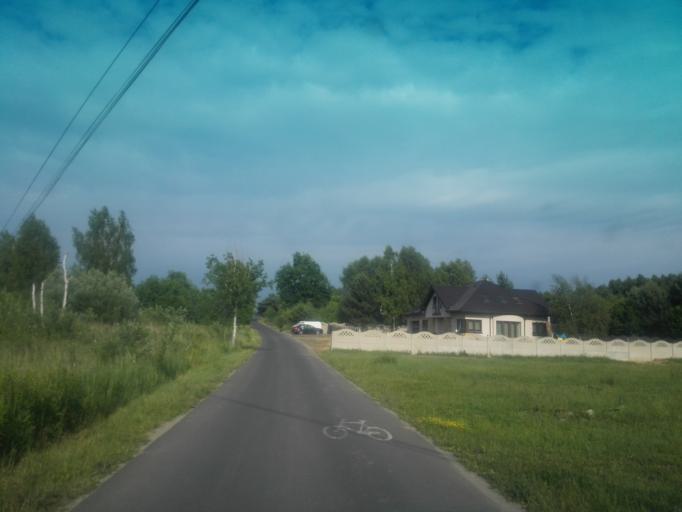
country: PL
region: Silesian Voivodeship
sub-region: Powiat czestochowski
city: Mstow
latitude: 50.8318
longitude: 19.3015
